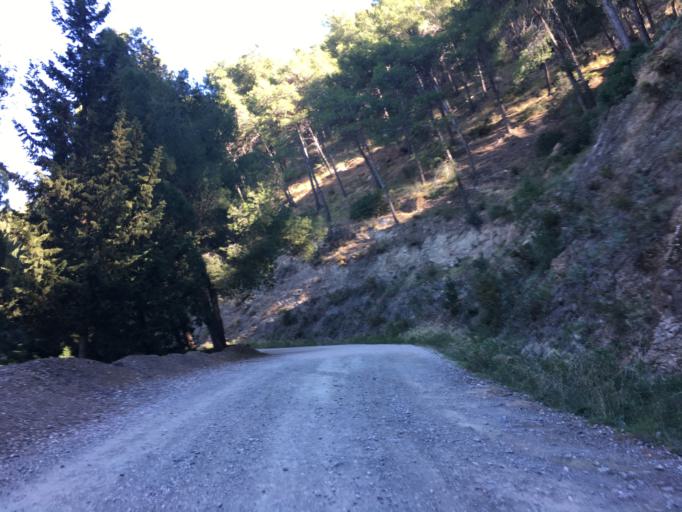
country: ES
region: Andalusia
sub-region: Provincia de Malaga
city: Malaga
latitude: 36.7741
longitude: -4.3847
